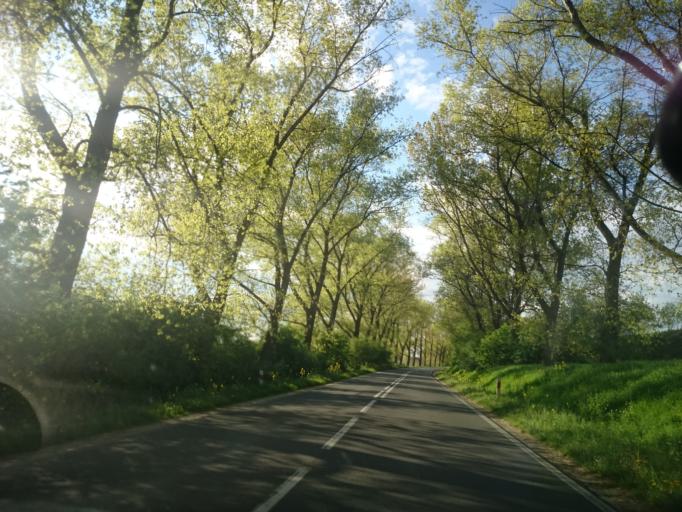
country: PL
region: Lower Silesian Voivodeship
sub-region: Powiat zabkowicki
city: Kamieniec Zabkowicki
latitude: 50.5456
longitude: 16.8614
